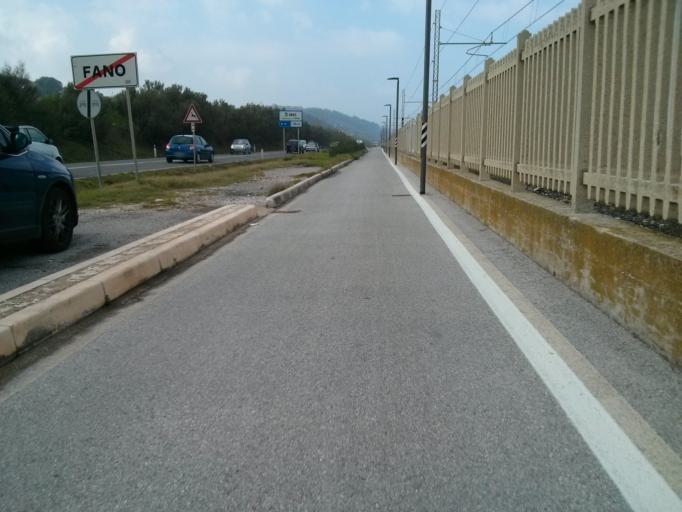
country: IT
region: The Marches
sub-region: Provincia di Pesaro e Urbino
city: Fenile
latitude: 43.8631
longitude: 12.9895
